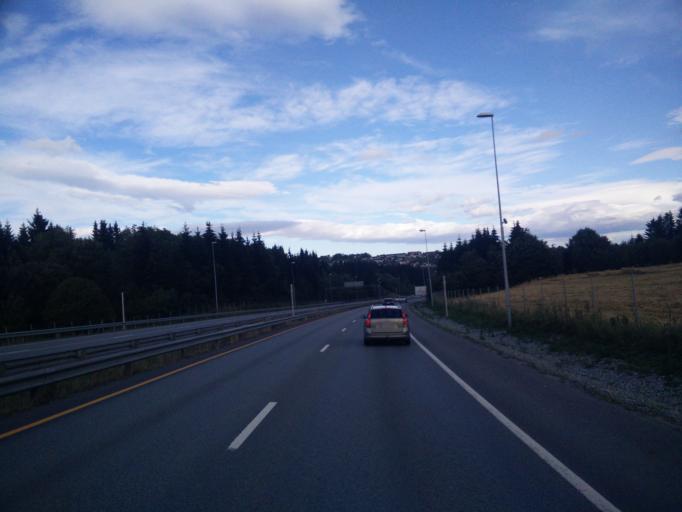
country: NO
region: Sor-Trondelag
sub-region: Trondheim
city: Trondheim
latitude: 63.3783
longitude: 10.3754
